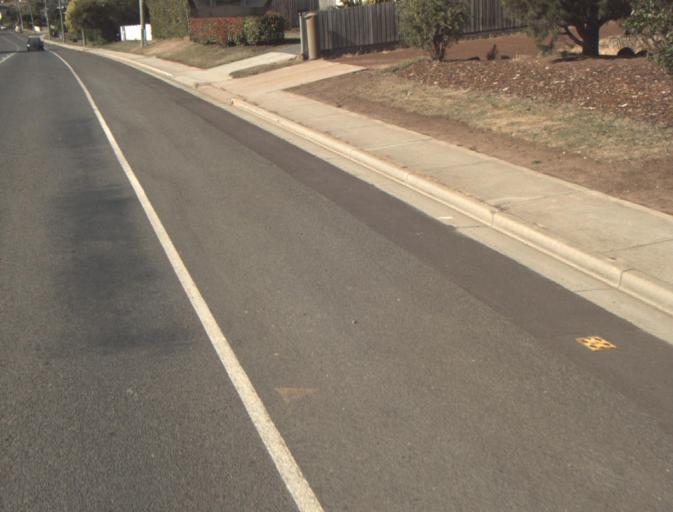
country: AU
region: Tasmania
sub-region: Launceston
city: Mayfield
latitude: -41.3745
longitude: 147.1340
